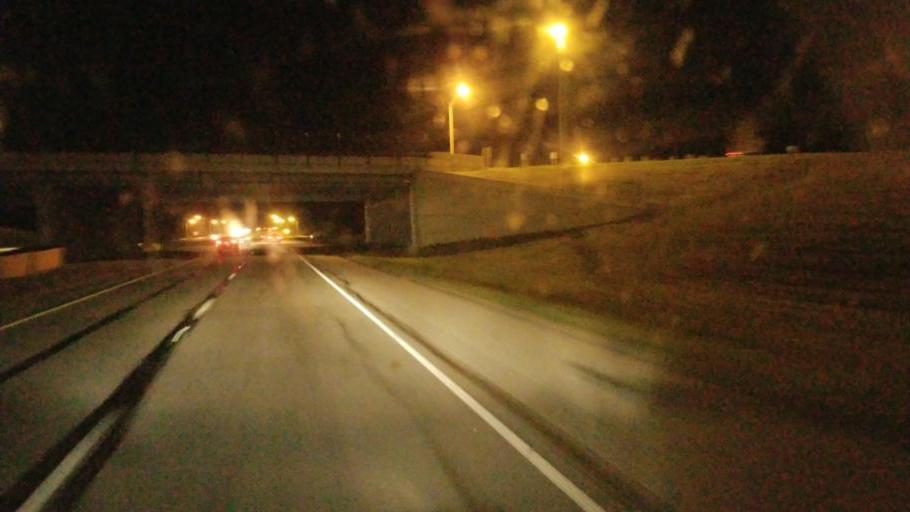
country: US
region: Indiana
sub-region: Allen County
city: Fort Wayne
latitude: 41.1996
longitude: -85.1040
